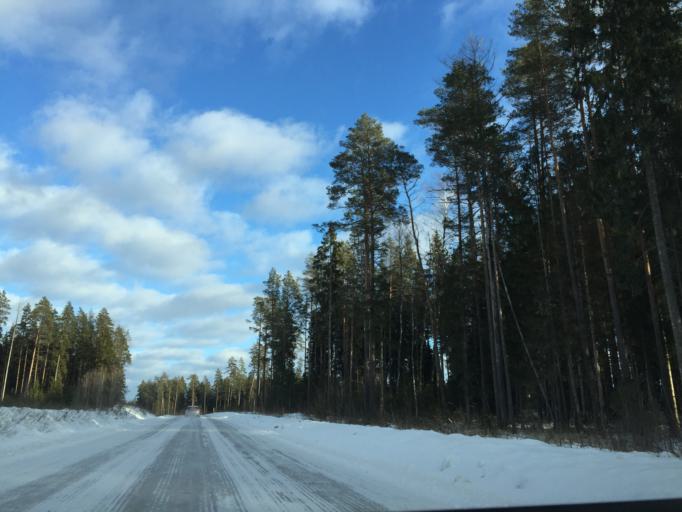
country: LV
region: Ogre
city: Jumprava
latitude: 56.5893
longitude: 24.9740
